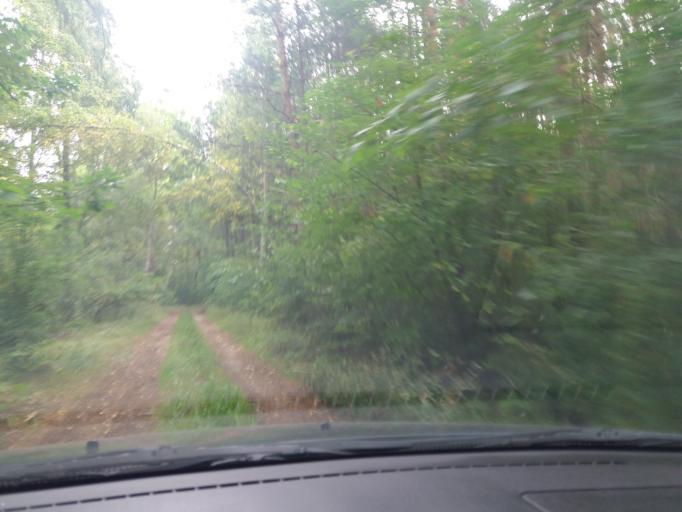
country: PL
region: Masovian Voivodeship
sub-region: Powiat mlawski
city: Wieczfnia Koscielna
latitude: 53.2223
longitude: 20.4629
